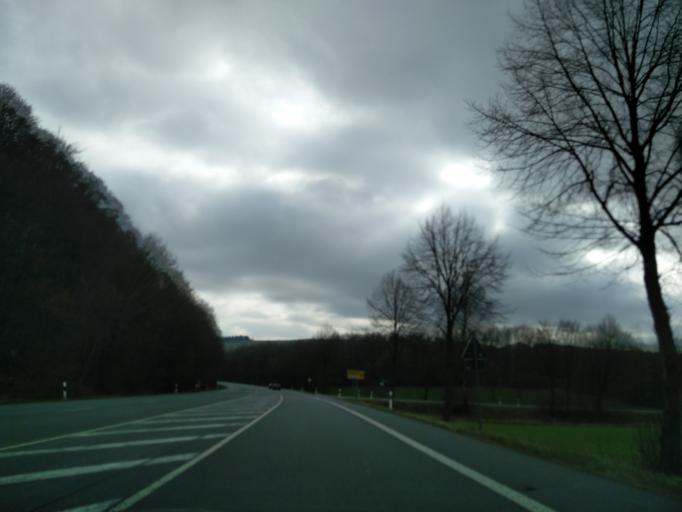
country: DE
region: North Rhine-Westphalia
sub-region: Regierungsbezirk Detmold
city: Willebadessen
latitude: 51.5447
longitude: 9.0112
